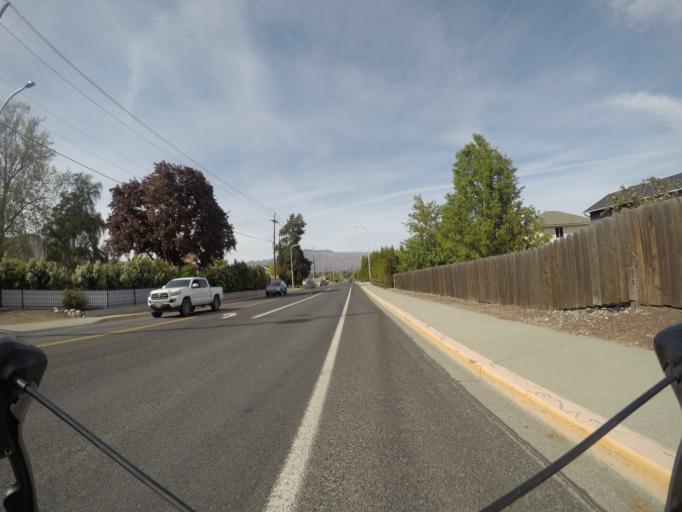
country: US
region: Washington
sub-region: Chelan County
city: West Wenatchee
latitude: 47.4183
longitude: -120.3458
